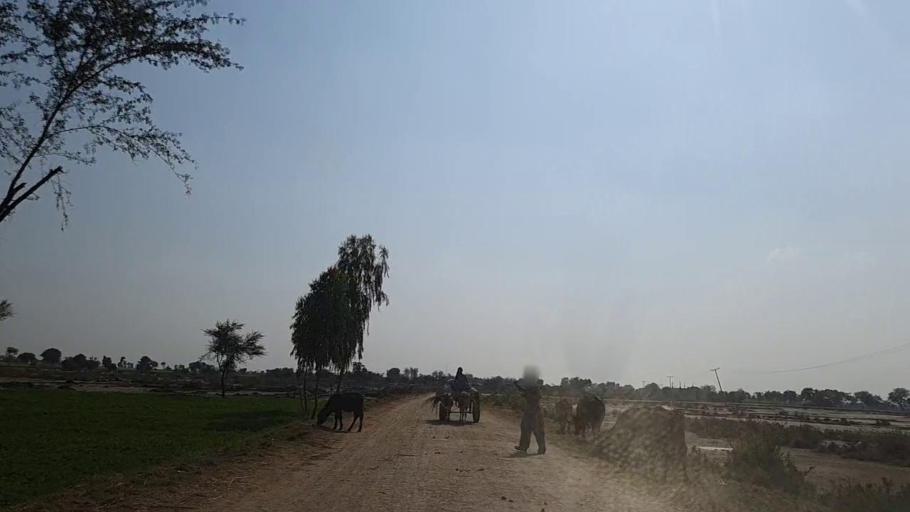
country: PK
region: Sindh
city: Daur
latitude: 26.4554
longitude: 68.2502
